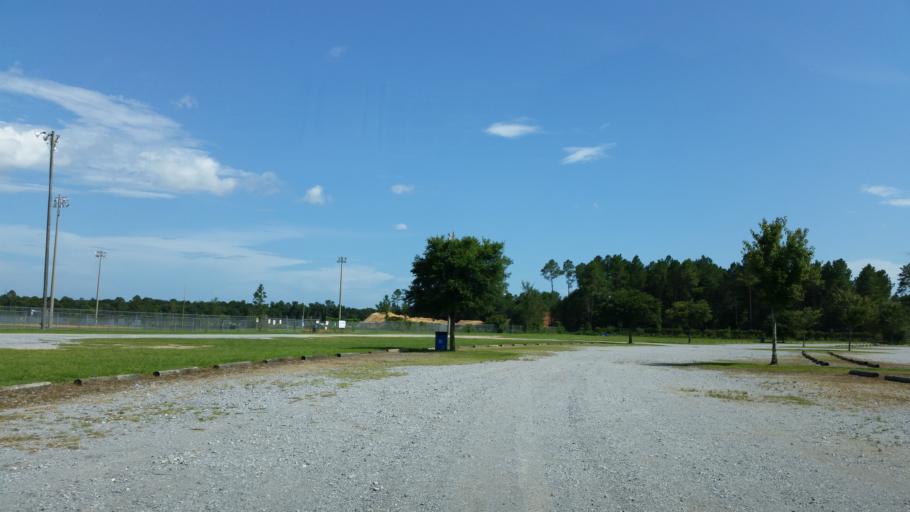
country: US
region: Florida
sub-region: Escambia County
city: Ensley
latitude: 30.5306
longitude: -87.2550
